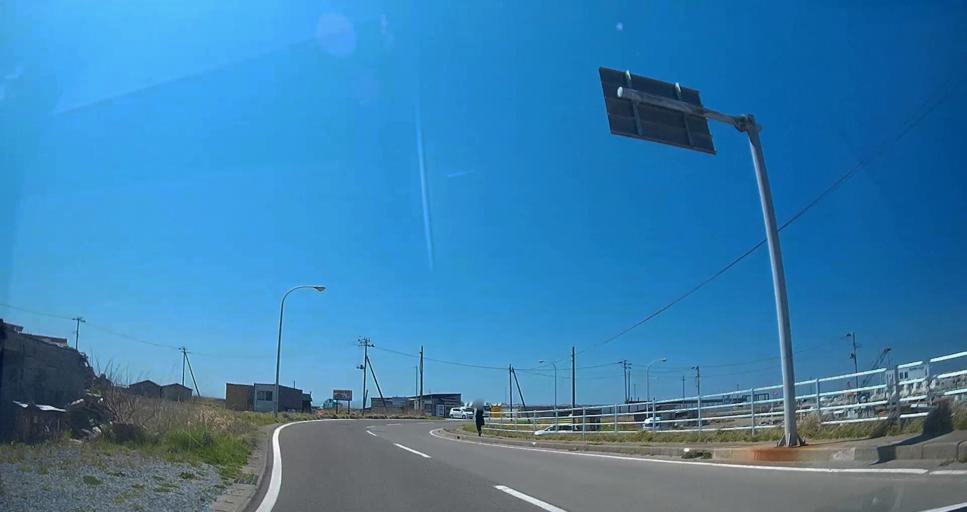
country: JP
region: Hokkaido
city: Hakodate
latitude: 41.5243
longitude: 140.9004
